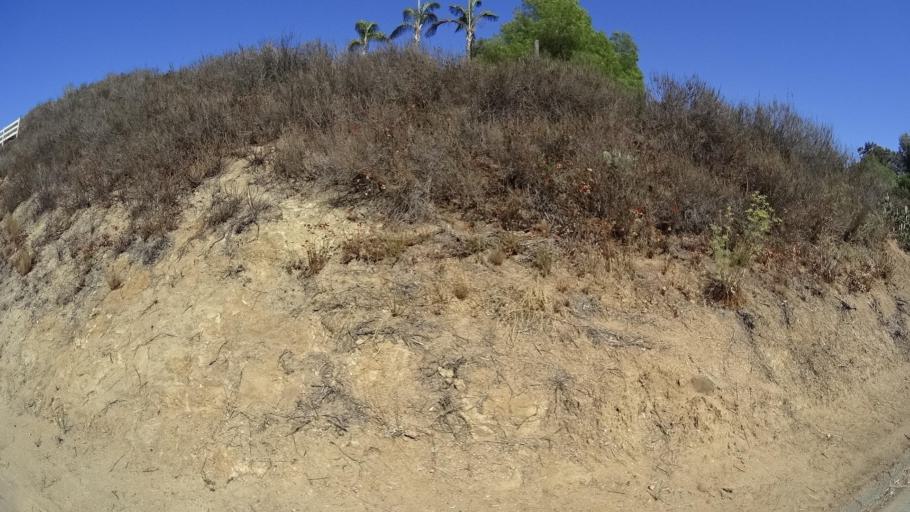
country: US
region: California
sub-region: San Diego County
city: Bonsall
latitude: 33.2917
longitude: -117.2167
